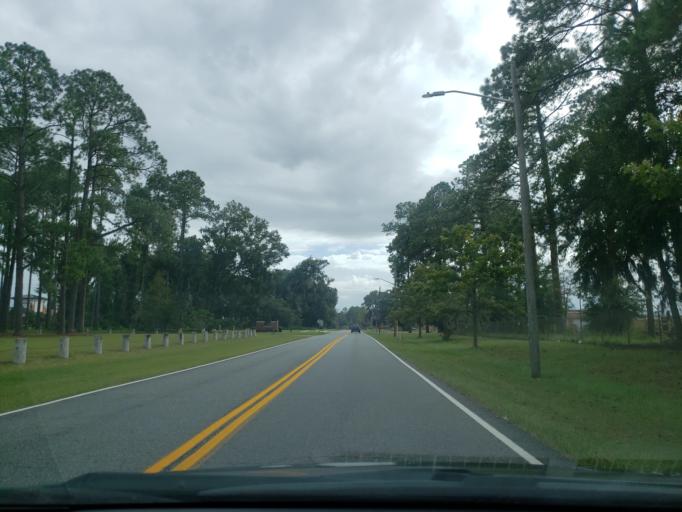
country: US
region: Georgia
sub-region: Chatham County
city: Isle of Hope
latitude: 32.0099
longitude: -81.0947
